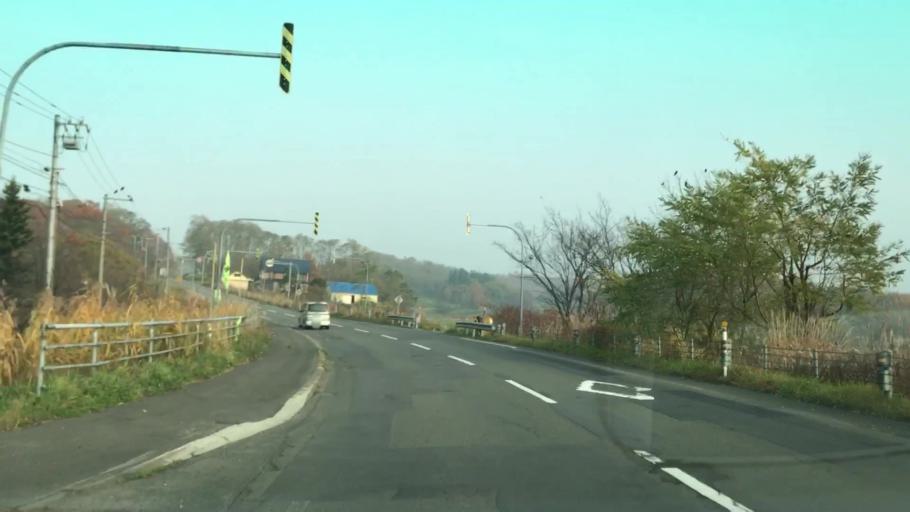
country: JP
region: Hokkaido
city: Ishikari
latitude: 43.3243
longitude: 141.4434
